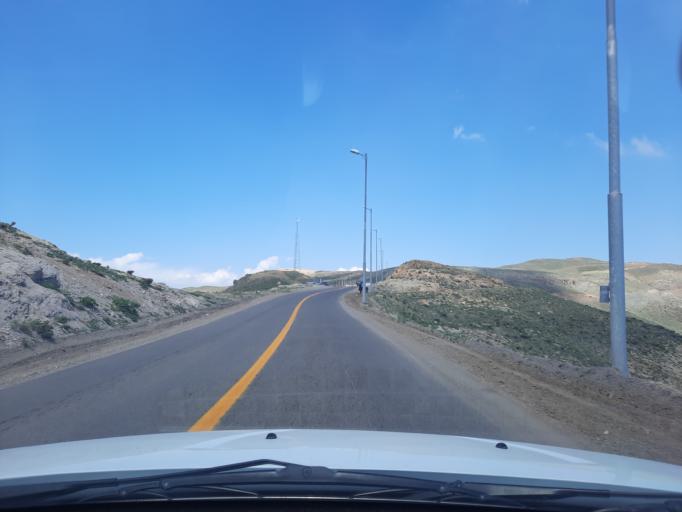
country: IR
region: Qazvin
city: Qazvin
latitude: 36.3816
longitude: 50.2030
